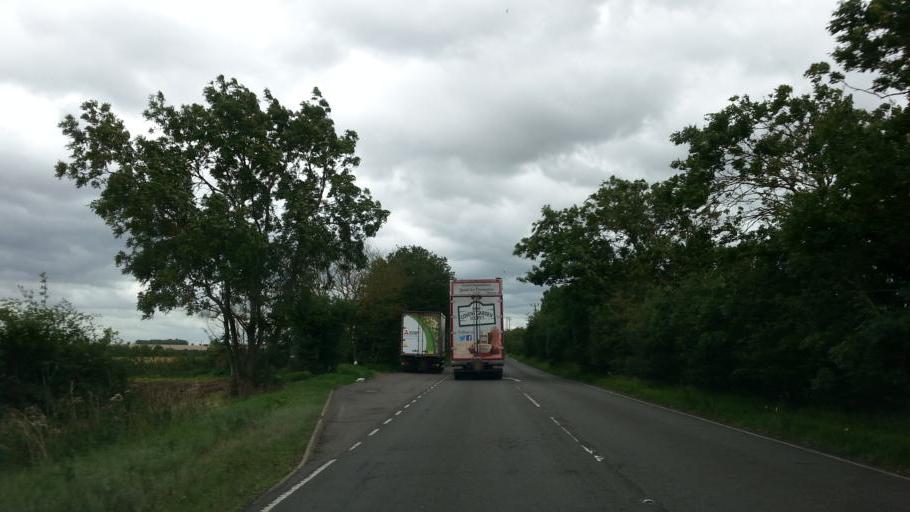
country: GB
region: England
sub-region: Cambridgeshire
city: Papworth Everard
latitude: 52.2673
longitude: -0.1312
